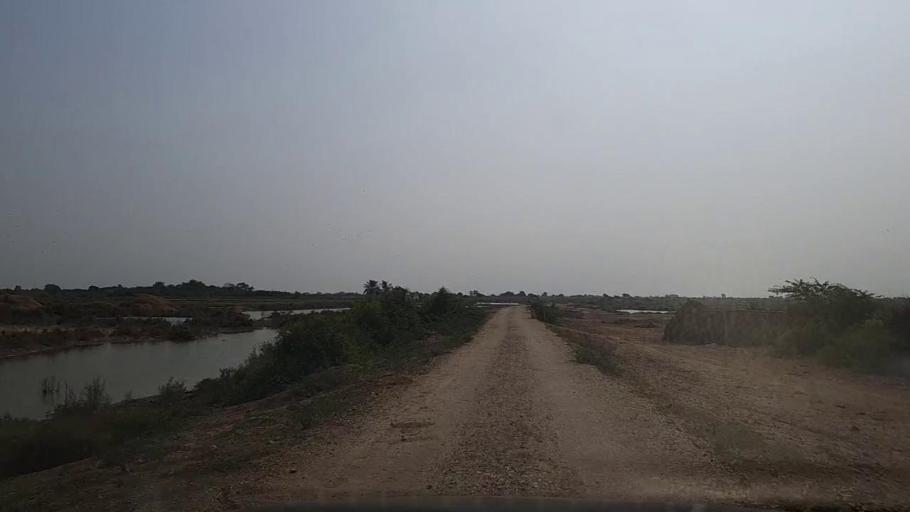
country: PK
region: Sindh
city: Thatta
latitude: 24.5716
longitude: 67.9167
